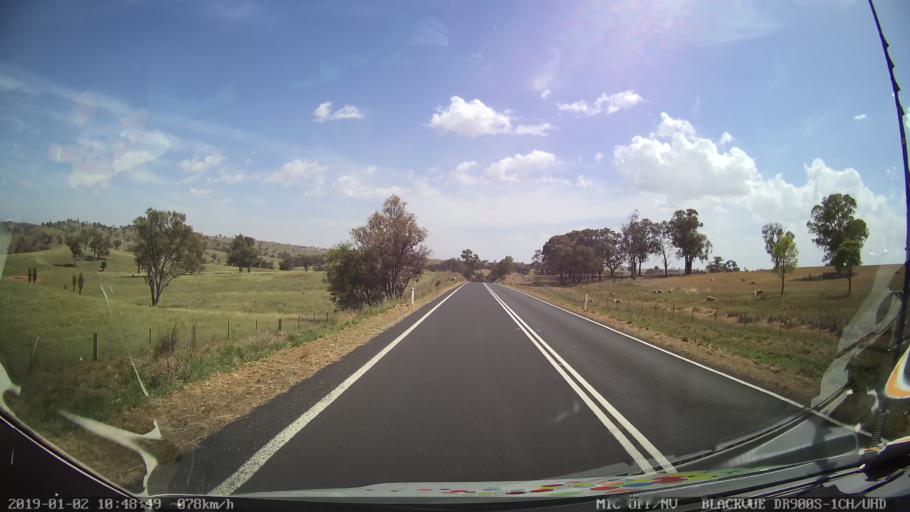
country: AU
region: New South Wales
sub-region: Cootamundra
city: Cootamundra
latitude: -34.7324
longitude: 148.2776
